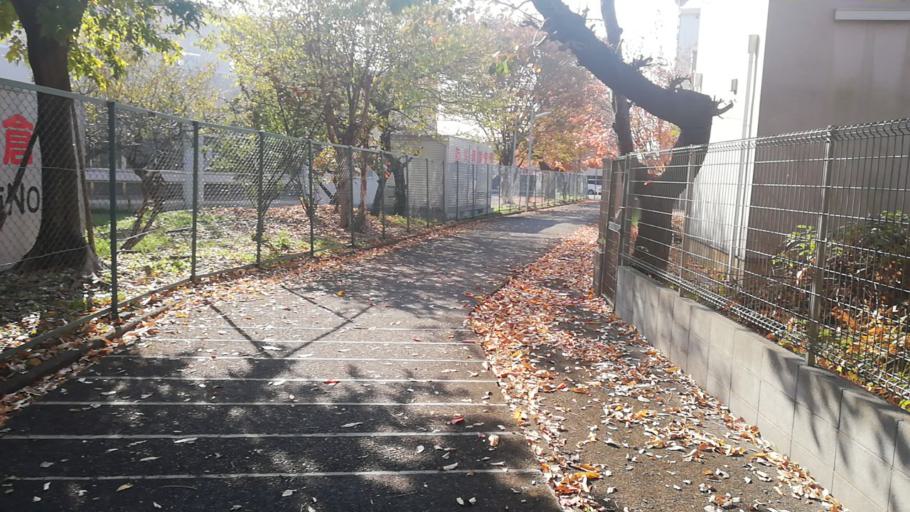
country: JP
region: Tokyo
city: Chofugaoka
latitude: 35.6607
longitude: 139.5552
